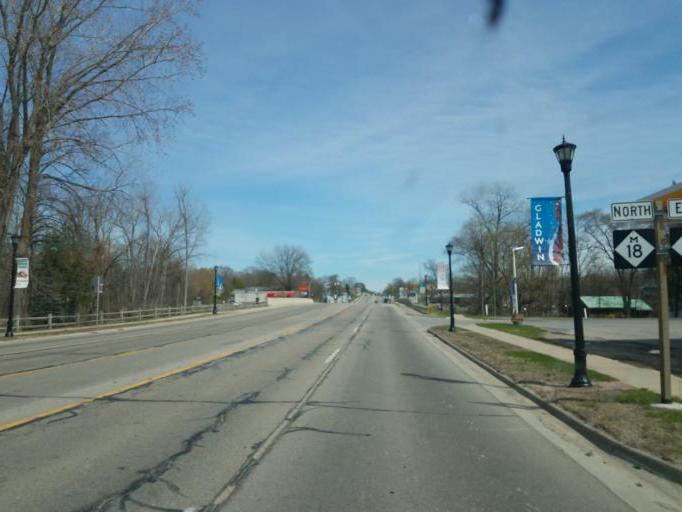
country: US
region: Michigan
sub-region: Gladwin County
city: Gladwin
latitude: 43.9808
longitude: -84.4978
